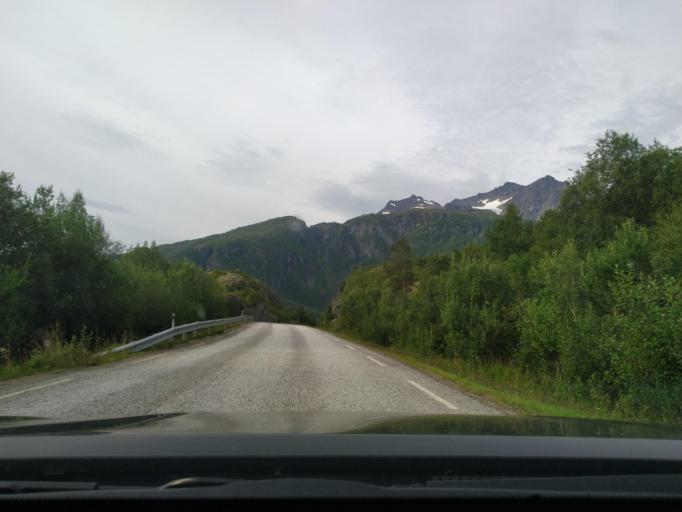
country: NO
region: Troms
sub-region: Dyroy
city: Brostadbotn
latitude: 68.8978
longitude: 17.4700
